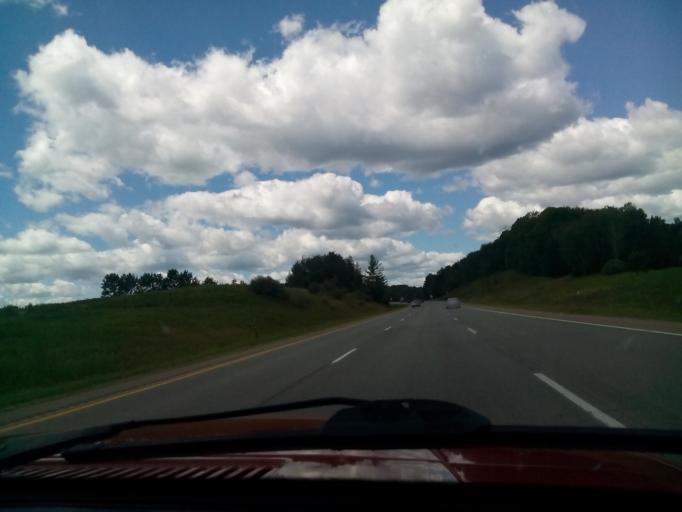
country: US
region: Michigan
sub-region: Ogemaw County
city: West Branch
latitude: 44.2801
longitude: -84.2859
